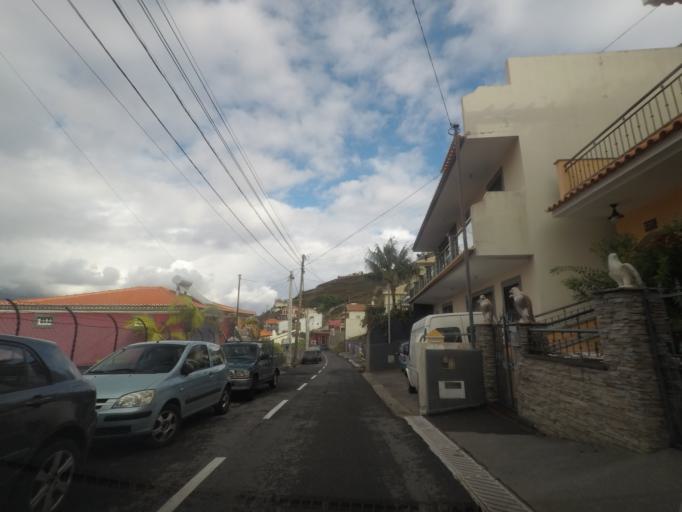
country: PT
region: Madeira
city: Camara de Lobos
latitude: 32.6560
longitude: -16.9956
